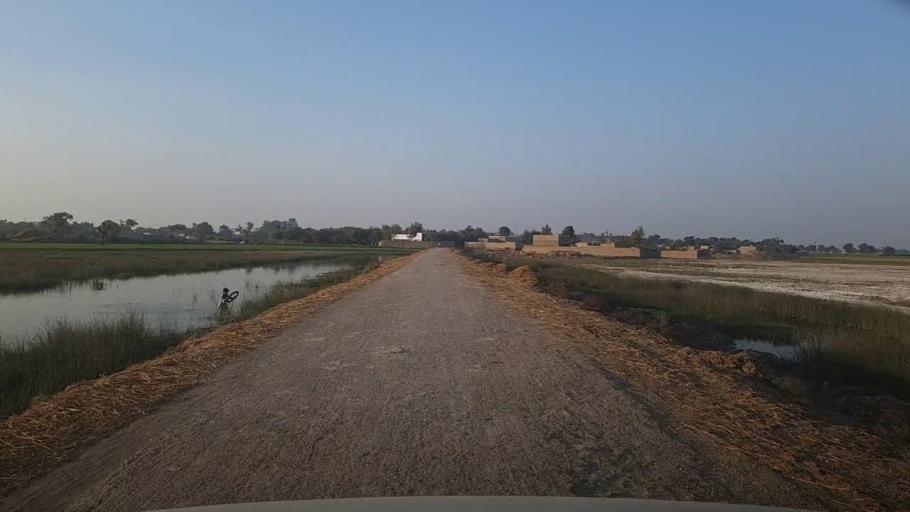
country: PK
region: Sindh
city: Mehar
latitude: 27.1963
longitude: 67.7819
